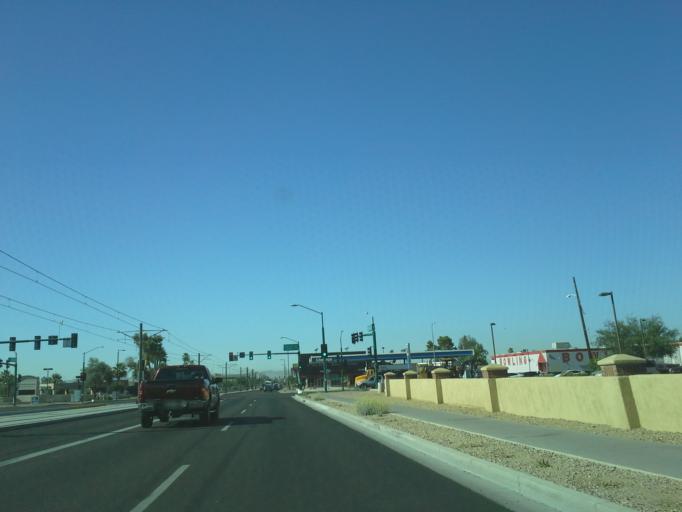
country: US
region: Arizona
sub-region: Maricopa County
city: Phoenix
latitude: 33.5250
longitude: -112.0999
